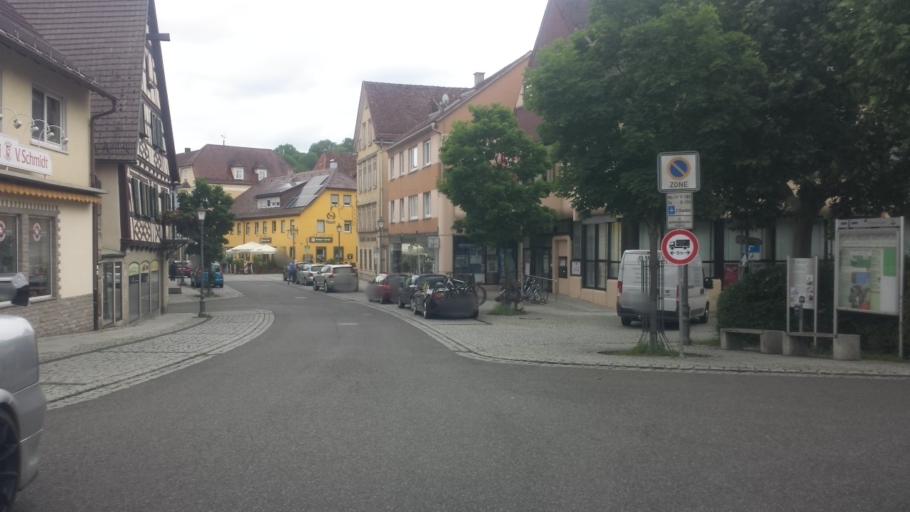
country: DE
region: Baden-Wuerttemberg
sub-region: Regierungsbezirk Stuttgart
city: Creglingen
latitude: 49.4701
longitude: 10.0312
